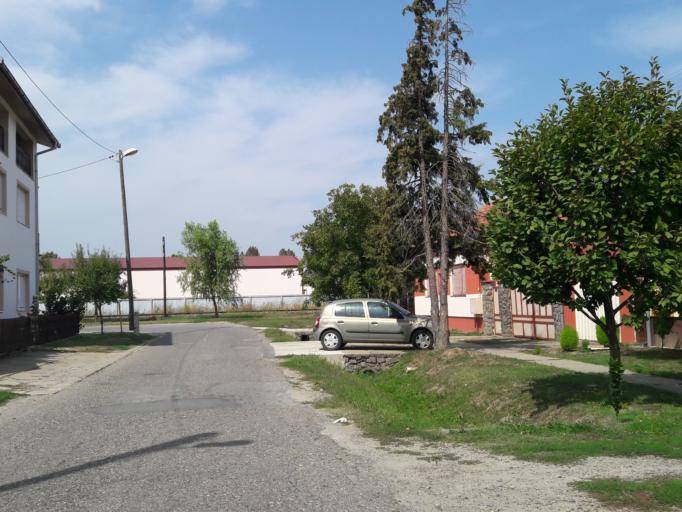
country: HR
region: Osjecko-Baranjska
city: Visnjevac
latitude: 45.5298
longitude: 18.6276
